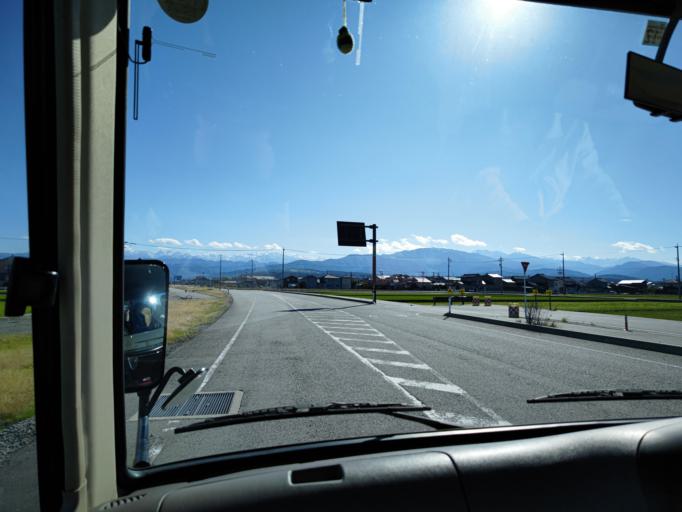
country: JP
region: Toyama
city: Nyuzen
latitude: 36.8823
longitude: 137.4362
